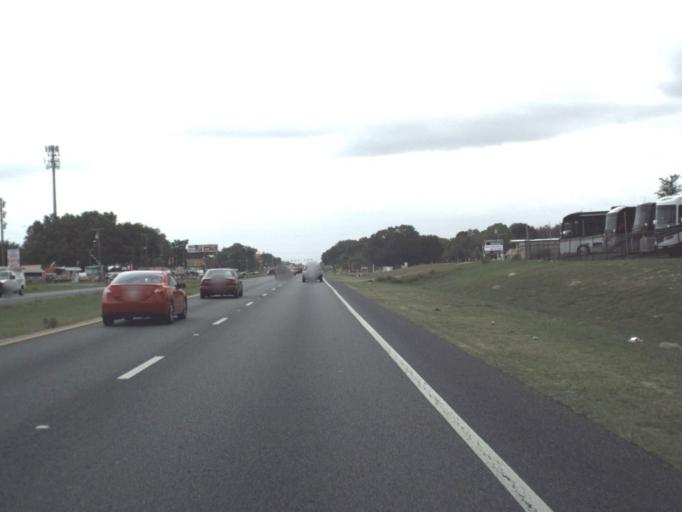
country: US
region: Florida
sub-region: Marion County
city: Belleview
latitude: 29.0146
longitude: -82.0114
